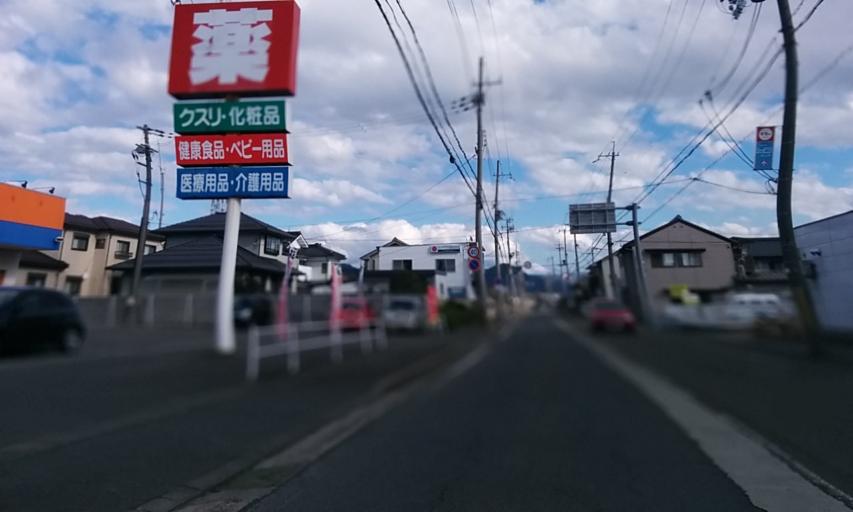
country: JP
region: Fukui
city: Obama
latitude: 35.4993
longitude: 135.7465
